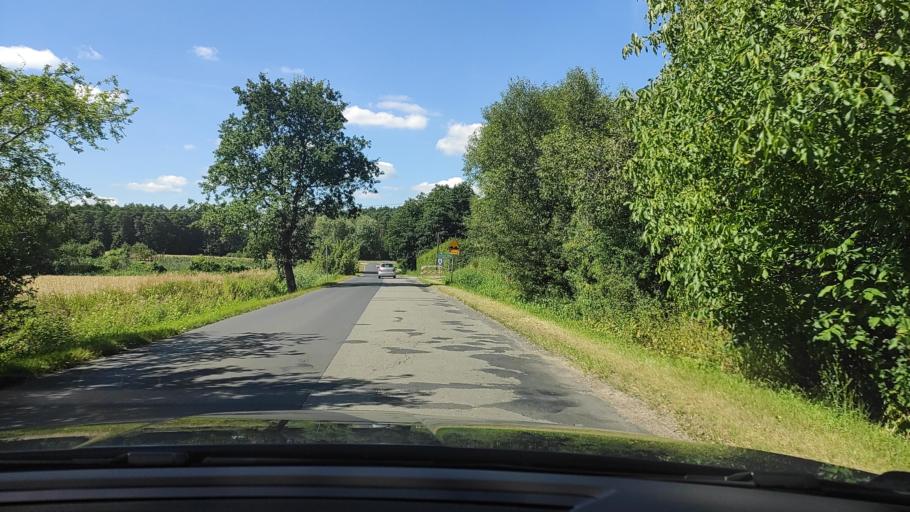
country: PL
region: Greater Poland Voivodeship
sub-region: Powiat poznanski
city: Kostrzyn
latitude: 52.4487
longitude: 17.1632
